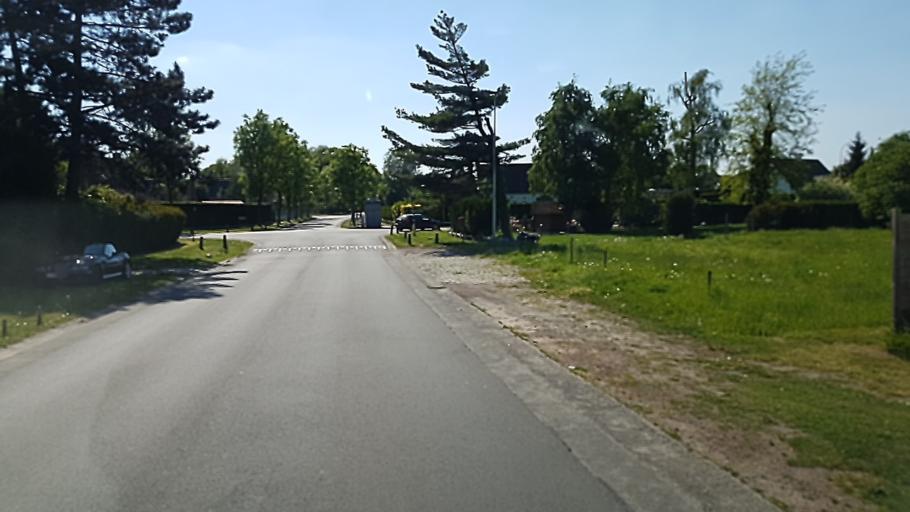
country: BE
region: Flanders
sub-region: Provincie Oost-Vlaanderen
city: Destelbergen
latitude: 51.0784
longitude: 3.7968
